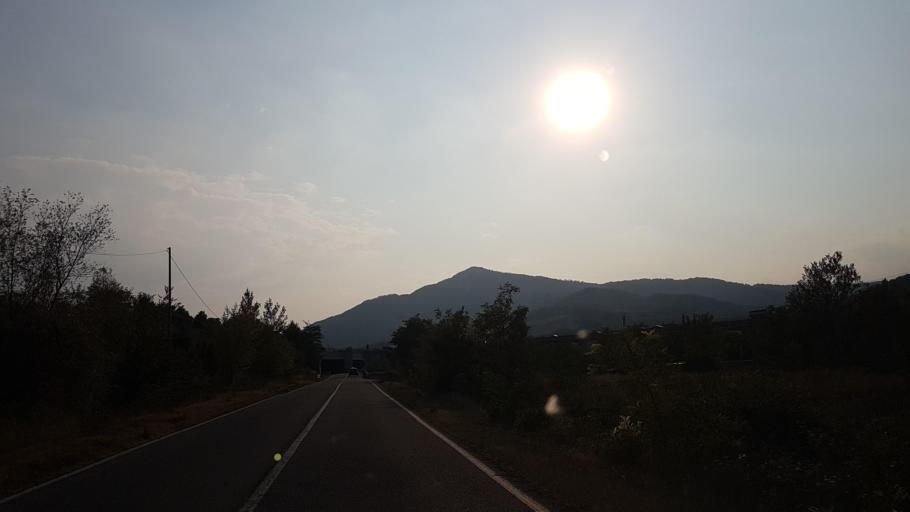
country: IT
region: Emilia-Romagna
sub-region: Provincia di Parma
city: Varano De' Melegari
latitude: 44.6541
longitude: 10.0531
